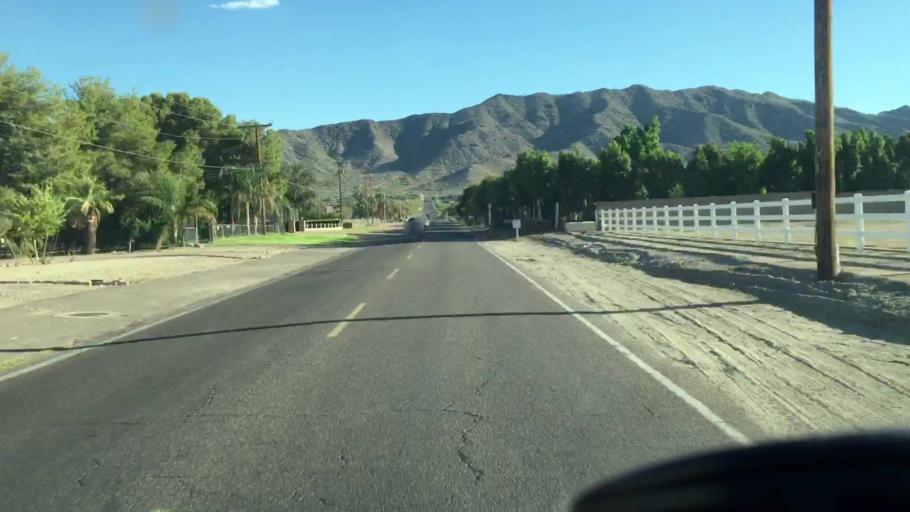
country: US
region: Arizona
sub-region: Maricopa County
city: Laveen
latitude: 33.3681
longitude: -112.0991
